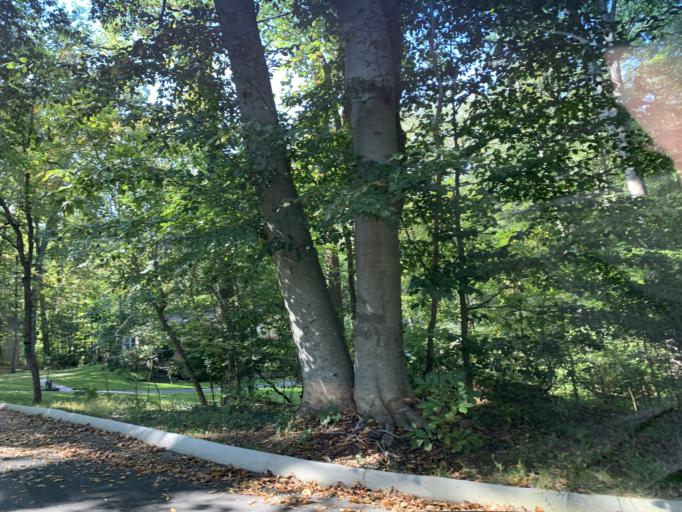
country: US
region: Maryland
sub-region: Harford County
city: South Bel Air
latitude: 39.5271
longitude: -76.3307
